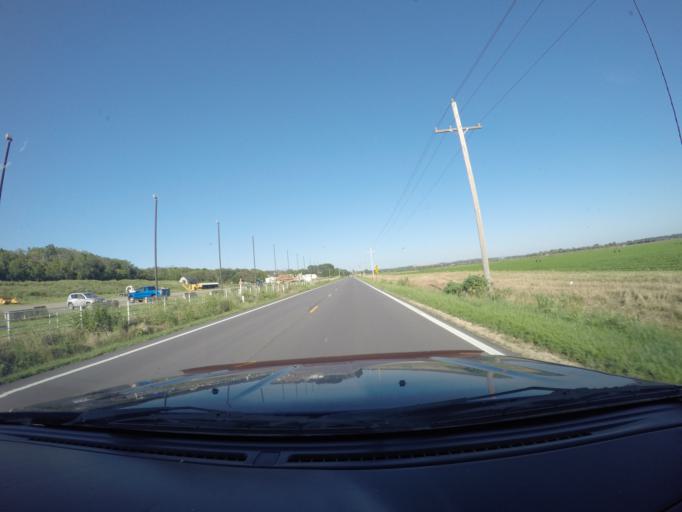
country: US
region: Kansas
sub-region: Douglas County
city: Lawrence
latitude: 39.0657
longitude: -95.3221
